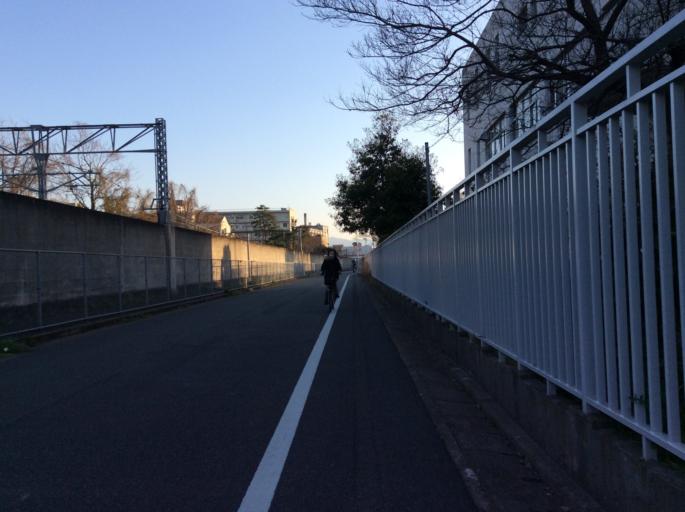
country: JP
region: Fukuoka
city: Fukuoka-shi
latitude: 33.6292
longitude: 130.4247
